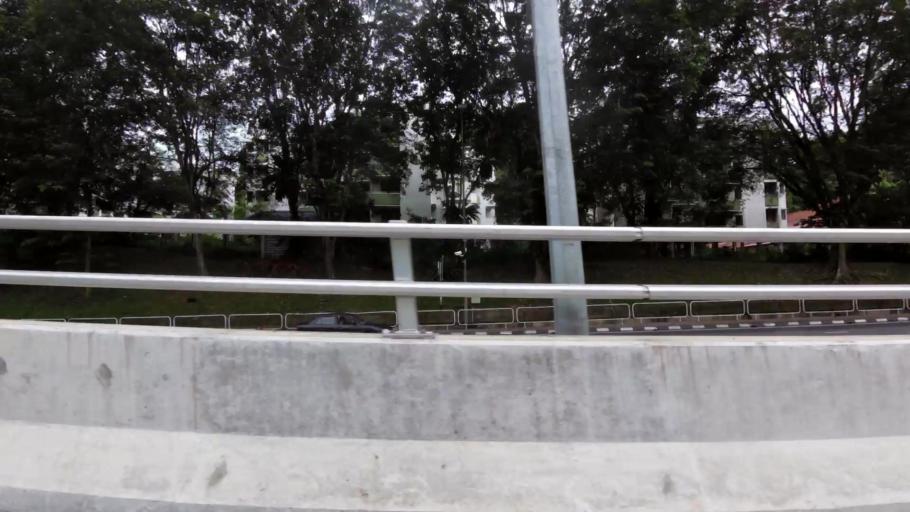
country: BN
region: Brunei and Muara
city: Bandar Seri Begawan
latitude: 4.8815
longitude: 114.9227
